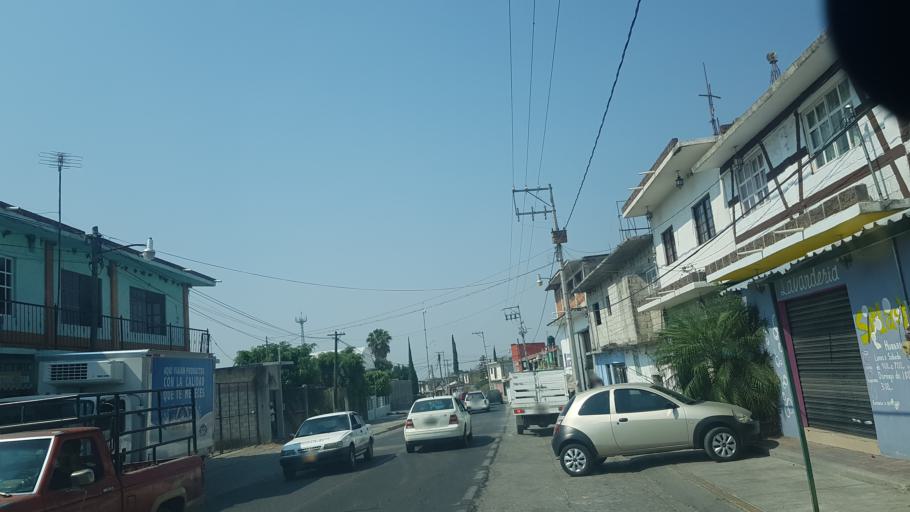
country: MX
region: Morelos
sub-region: Temoac
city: Temoac
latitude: 18.7768
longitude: -98.7759
